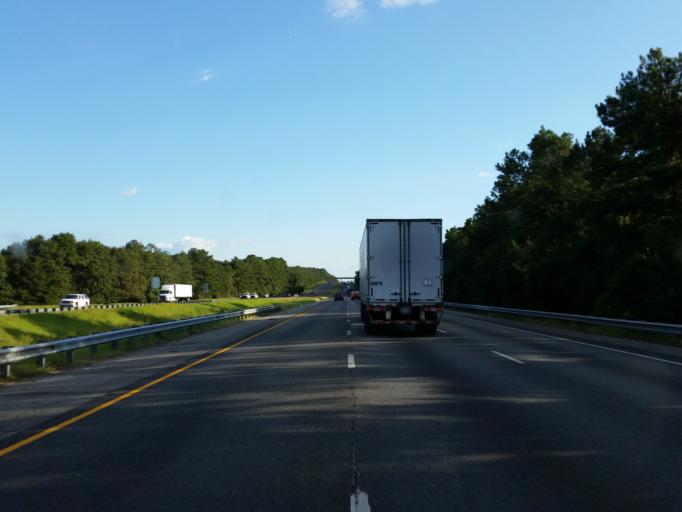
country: US
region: Georgia
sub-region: Houston County
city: Perry
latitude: 32.5215
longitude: -83.7436
